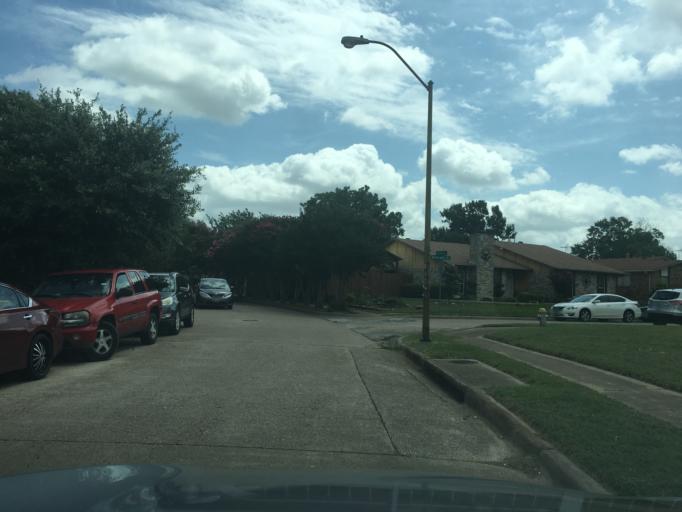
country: US
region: Texas
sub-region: Dallas County
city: Richardson
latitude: 32.9164
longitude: -96.7094
